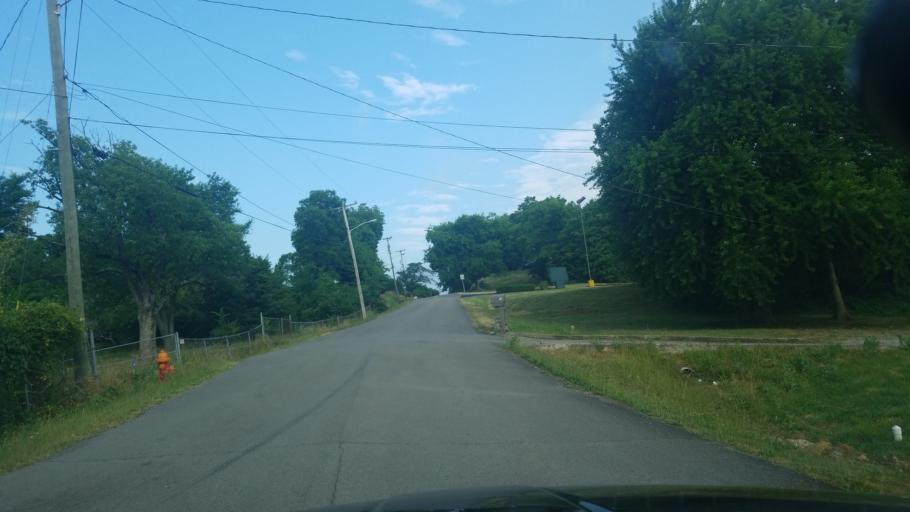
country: US
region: Tennessee
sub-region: Davidson County
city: Nashville
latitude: 36.2362
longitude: -86.7452
